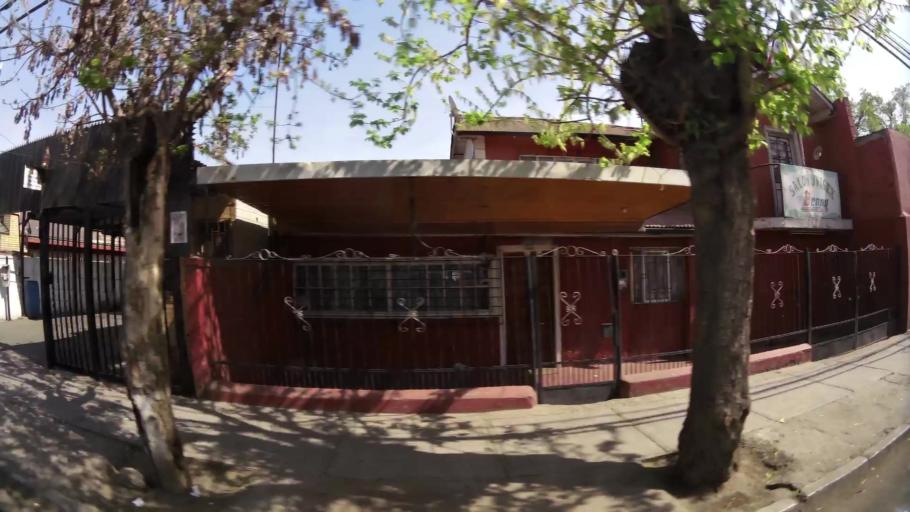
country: CL
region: Santiago Metropolitan
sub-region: Provincia de Santiago
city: Lo Prado
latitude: -33.4324
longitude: -70.7663
